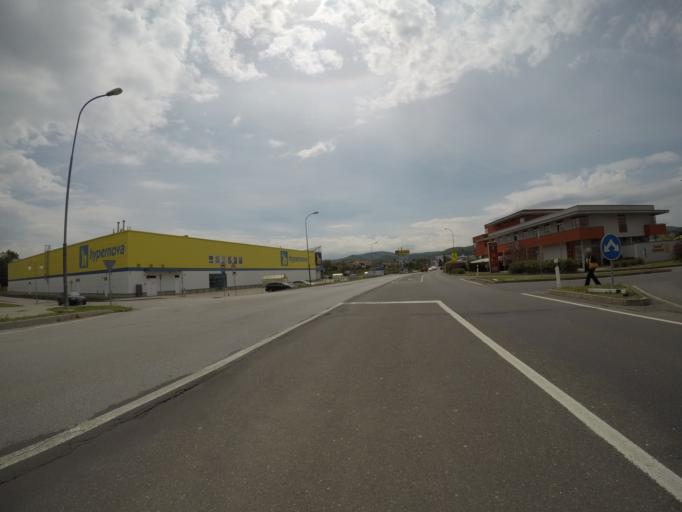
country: SK
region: Banskobystricky
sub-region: Okres Banska Bystrica
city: Zvolen
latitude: 48.5861
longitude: 19.1254
